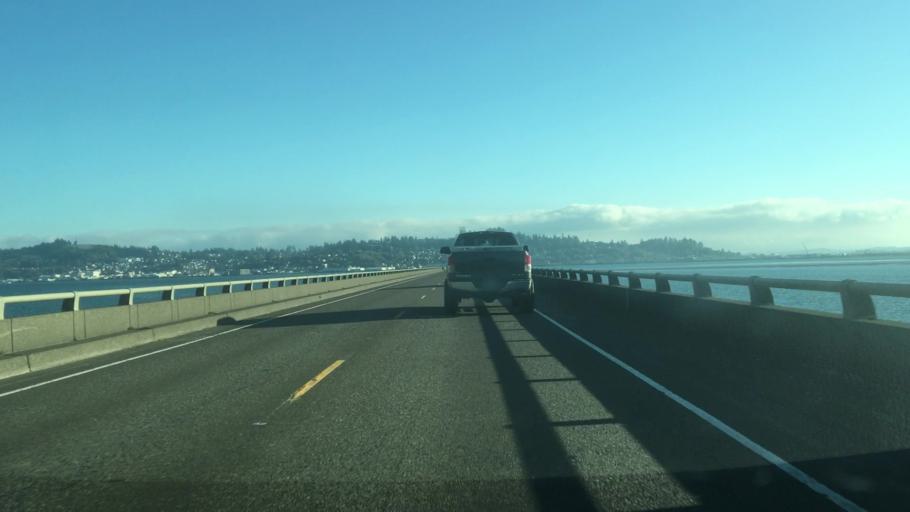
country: US
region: Oregon
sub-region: Clatsop County
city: Astoria
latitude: 46.2148
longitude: -123.8618
